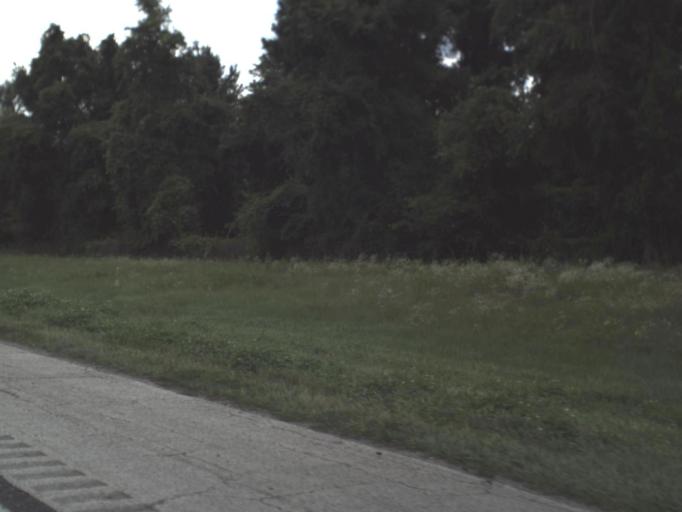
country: US
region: Florida
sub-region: Alachua County
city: Alachua
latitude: 29.7523
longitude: -82.4926
